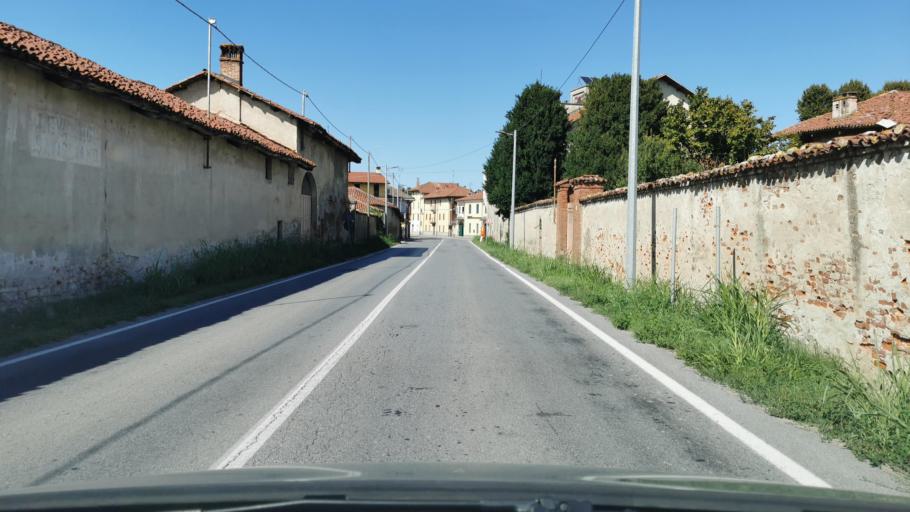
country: IT
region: Piedmont
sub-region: Provincia di Cuneo
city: Vottignasco
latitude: 44.5548
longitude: 7.6212
